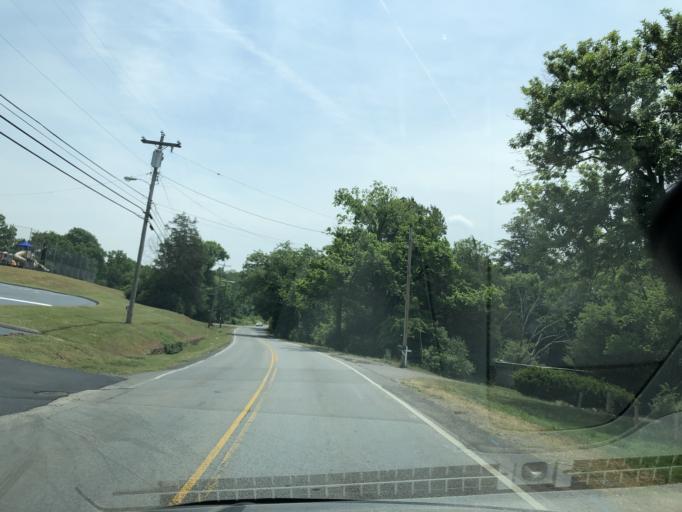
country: US
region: Tennessee
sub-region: Davidson County
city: Oak Hill
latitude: 36.0666
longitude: -86.6815
